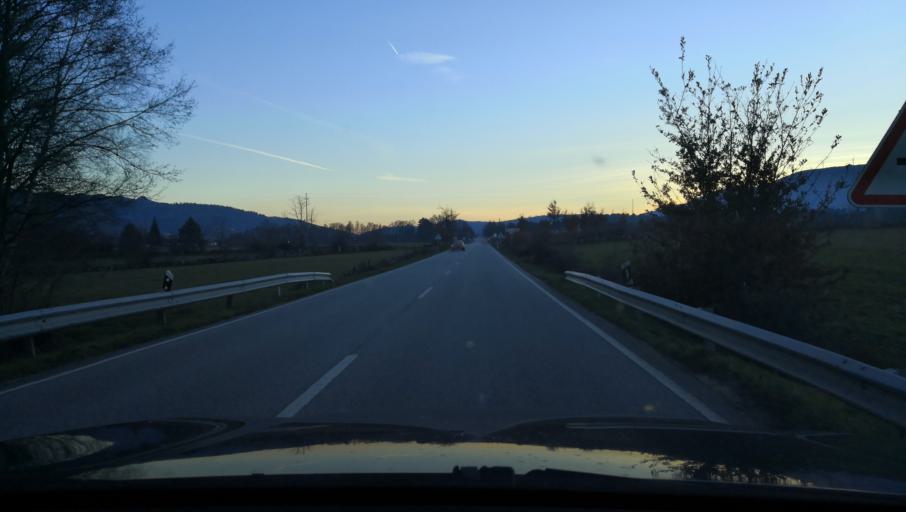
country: PT
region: Vila Real
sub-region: Vila Pouca de Aguiar
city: Vila Pouca de Aguiar
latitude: 41.4437
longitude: -7.6735
